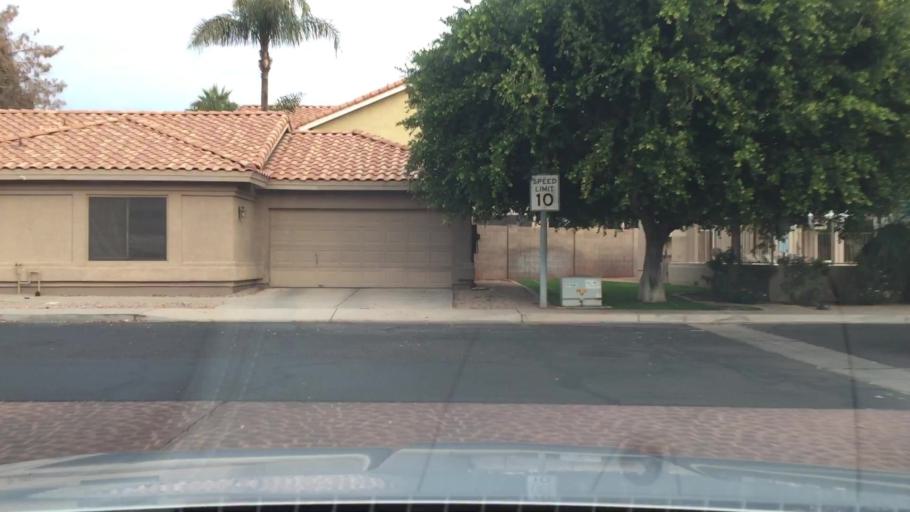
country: US
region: Arizona
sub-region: Maricopa County
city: Gilbert
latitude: 33.3753
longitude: -111.7914
